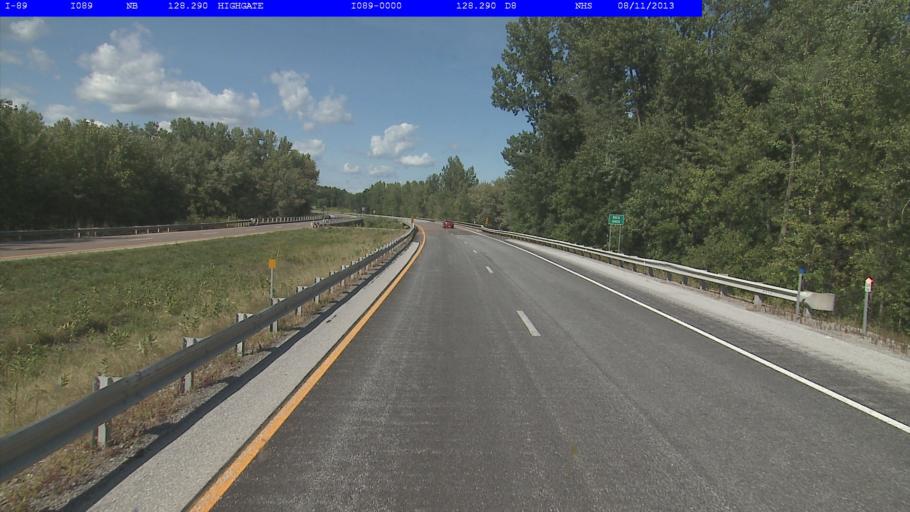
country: US
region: Vermont
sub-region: Franklin County
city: Swanton
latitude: 44.9875
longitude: -73.0872
